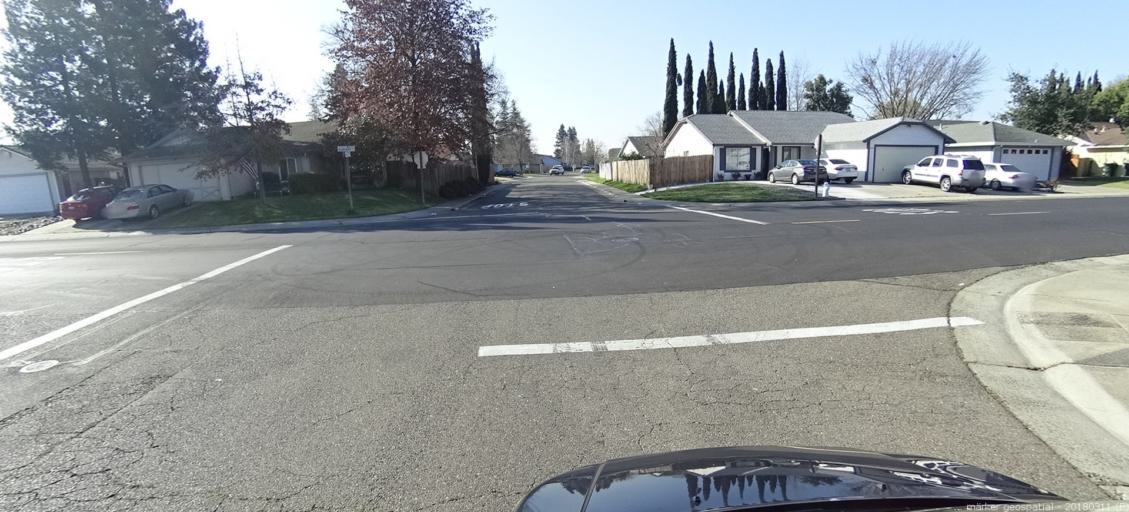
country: US
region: California
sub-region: Sacramento County
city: Florin
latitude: 38.4625
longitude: -121.4033
